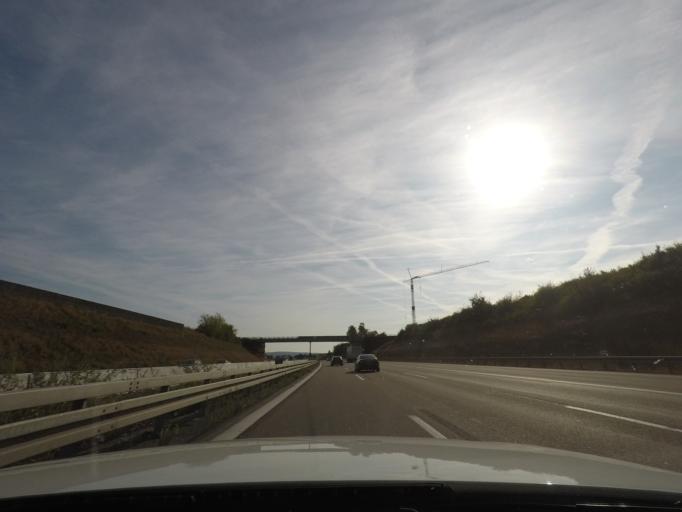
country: DE
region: Baden-Wuerttemberg
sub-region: Regierungsbezirk Stuttgart
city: Leingarten
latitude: 49.1858
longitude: 9.1311
